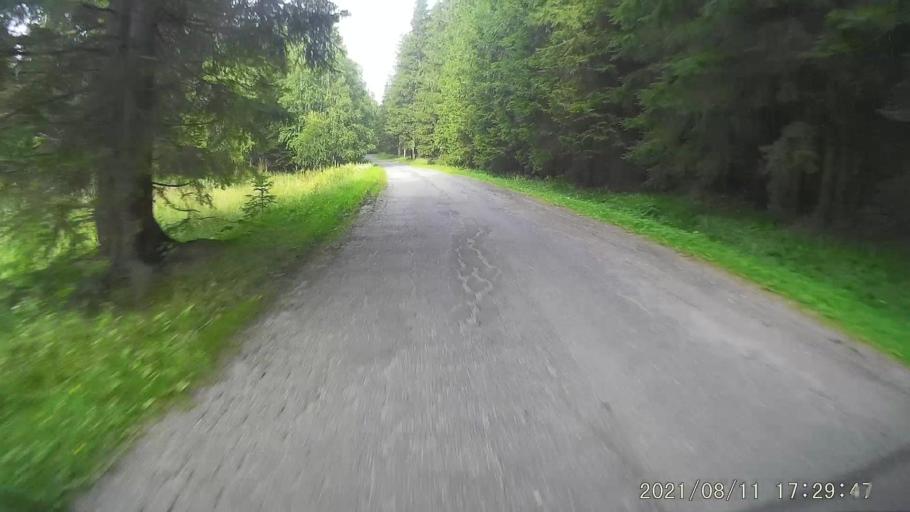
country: PL
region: Lower Silesian Voivodeship
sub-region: Powiat klodzki
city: Polanica-Zdroj
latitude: 50.2974
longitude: 16.4721
